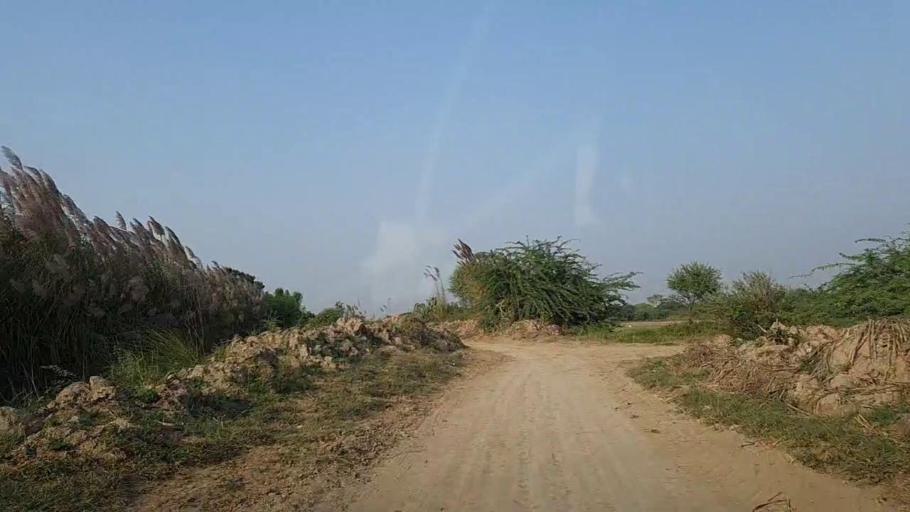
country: PK
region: Sindh
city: Mirpur Sakro
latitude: 24.6501
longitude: 67.7672
